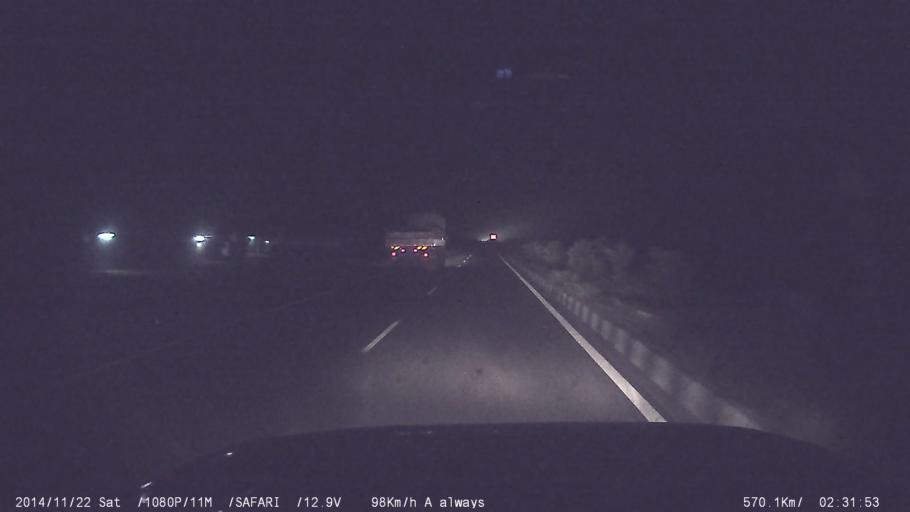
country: IN
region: Tamil Nadu
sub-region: Salem
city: Belur
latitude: 11.6570
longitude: 78.4300
